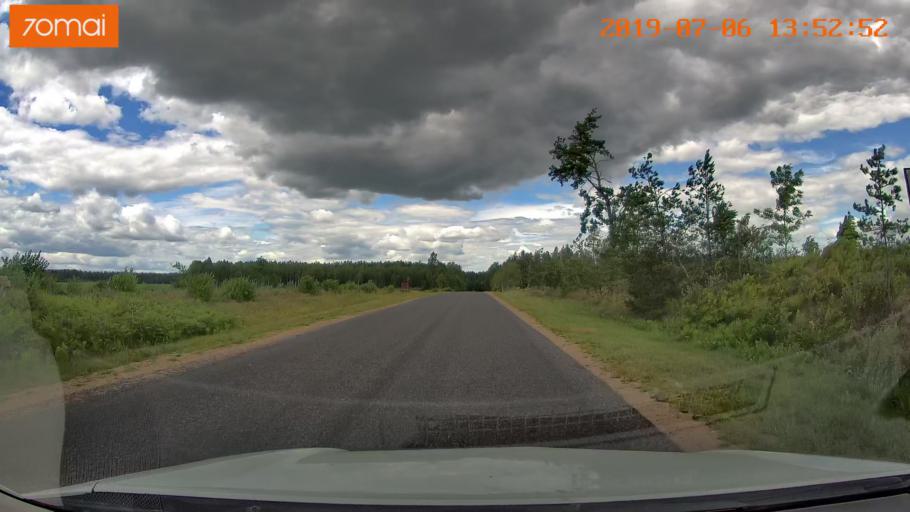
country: BY
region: Minsk
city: Ivyanyets
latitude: 53.7264
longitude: 26.8272
